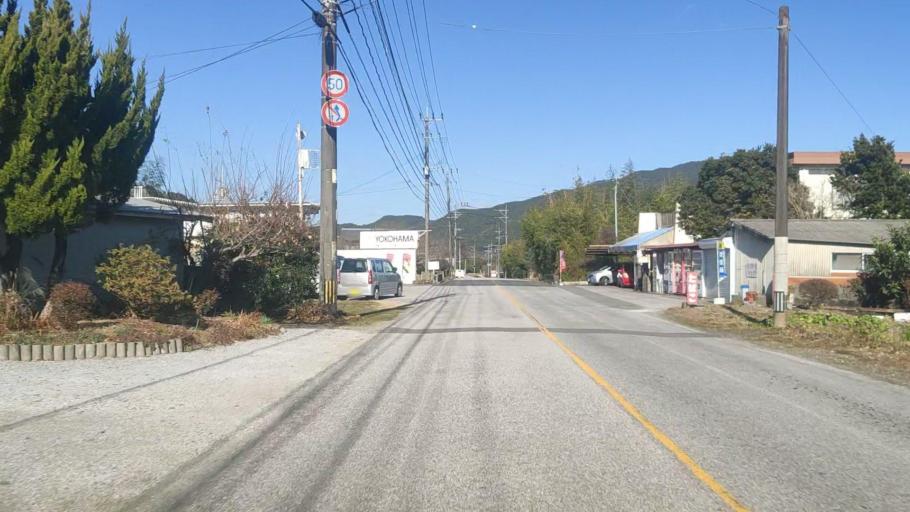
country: JP
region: Oita
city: Saiki
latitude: 32.9148
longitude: 131.9284
